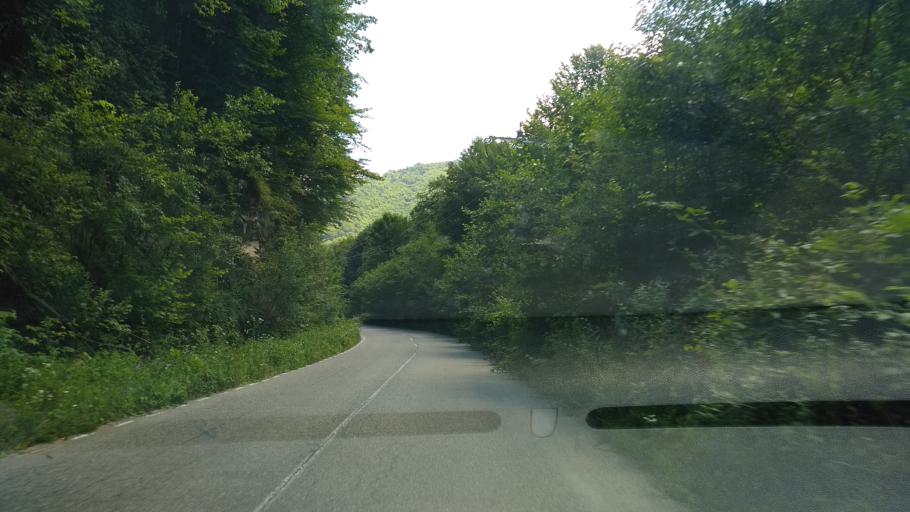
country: RO
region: Hunedoara
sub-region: Comuna Orastioara de Sus
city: Orastioara de Sus
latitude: 45.6662
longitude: 23.1711
